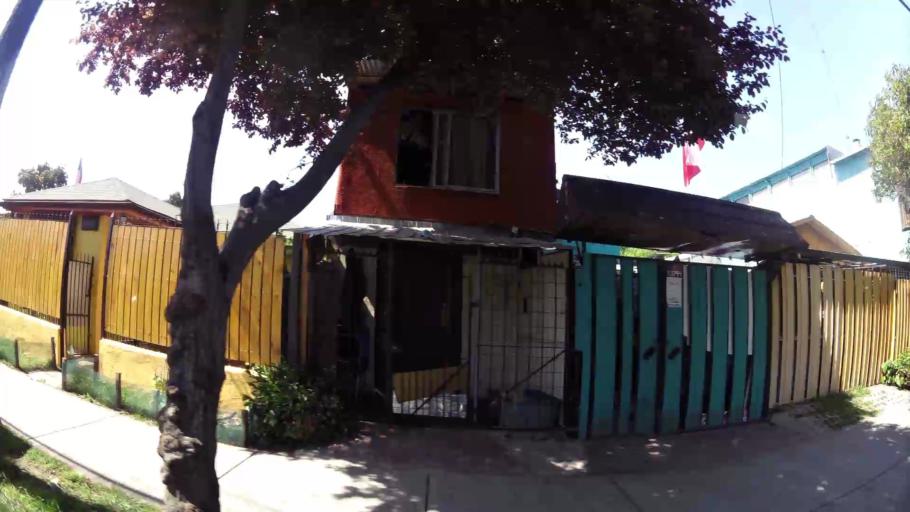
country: CL
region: Santiago Metropolitan
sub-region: Provincia de Santiago
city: La Pintana
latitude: -33.5537
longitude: -70.6659
